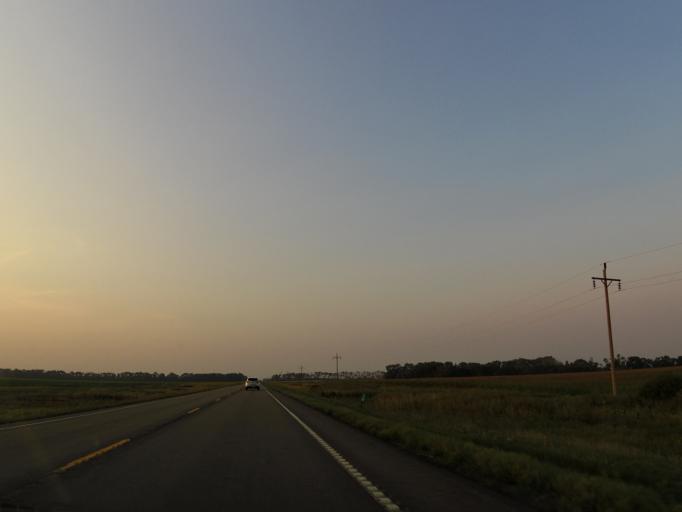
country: US
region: North Dakota
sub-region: Grand Forks County
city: Larimore
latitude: 48.0731
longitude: -97.6225
